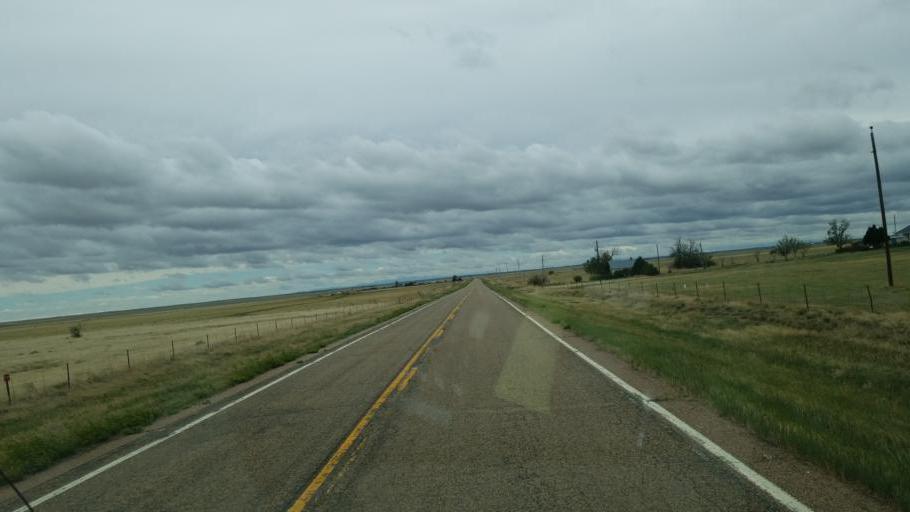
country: US
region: Colorado
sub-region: Lincoln County
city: Limon
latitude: 38.8386
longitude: -103.8767
